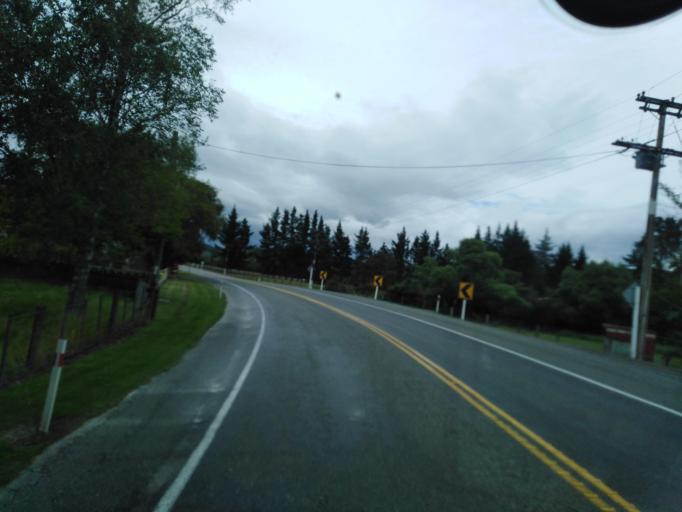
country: NZ
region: Tasman
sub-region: Tasman District
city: Wakefield
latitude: -41.4505
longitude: 172.9582
